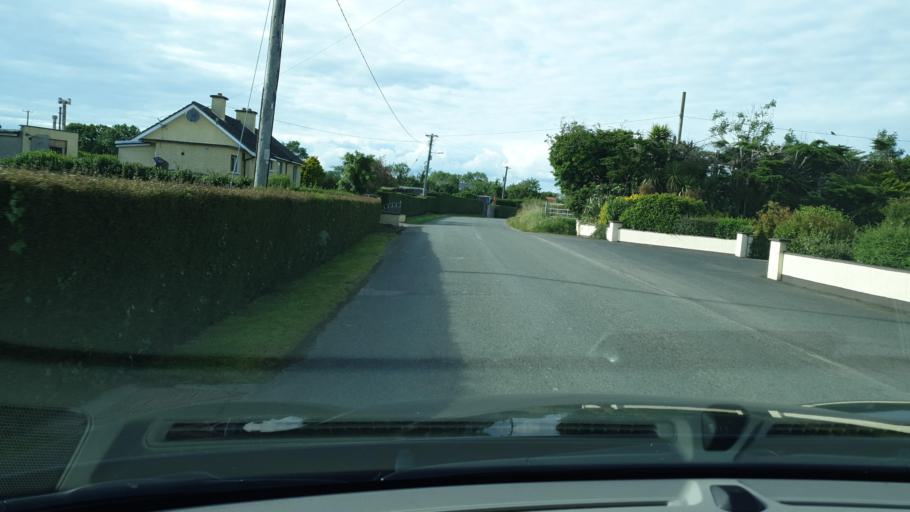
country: IE
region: Leinster
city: Balrothery
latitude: 53.5645
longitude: -6.1656
